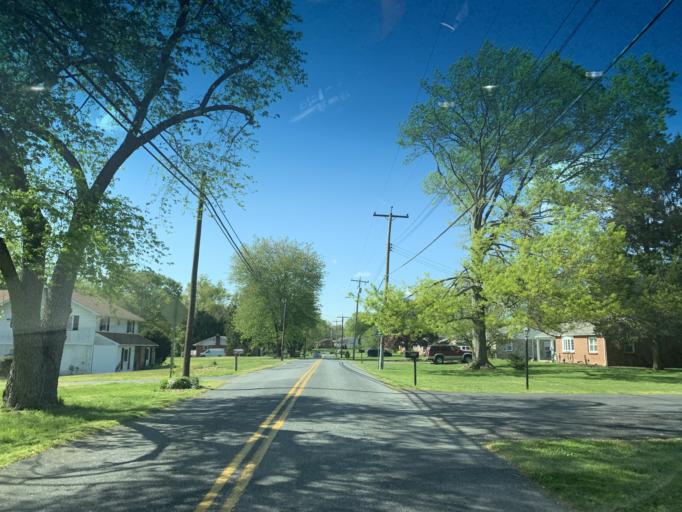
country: US
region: Maryland
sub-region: Harford County
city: Riverside
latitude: 39.4539
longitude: -76.2482
